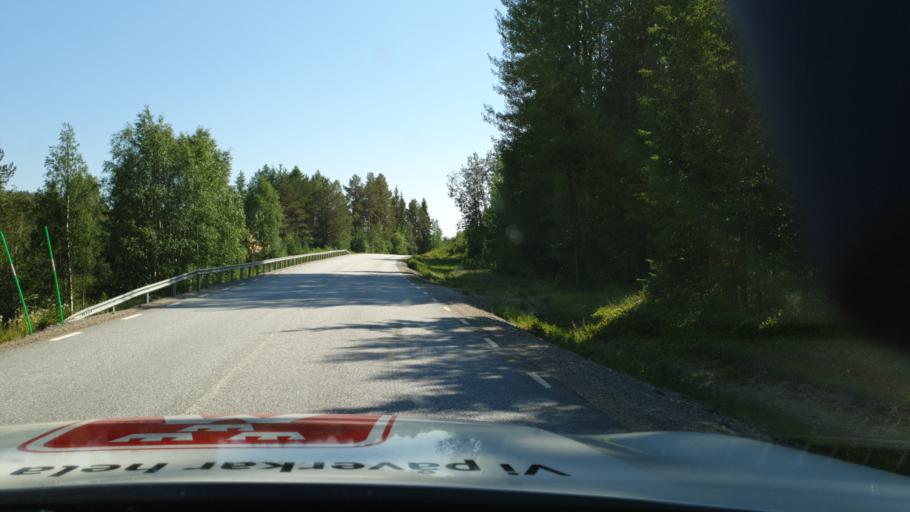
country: SE
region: Vaesterbotten
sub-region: Umea Kommun
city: Ersmark
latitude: 64.2956
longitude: 20.2247
